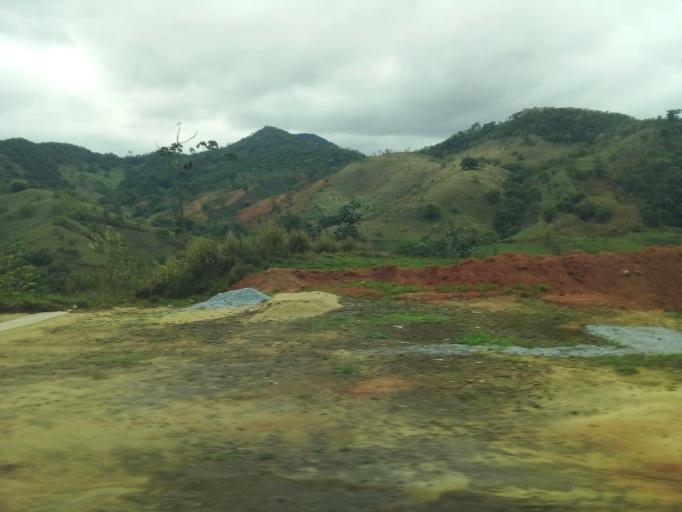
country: BR
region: Minas Gerais
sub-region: Nova Era
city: Nova Era
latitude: -19.6842
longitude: -42.9089
